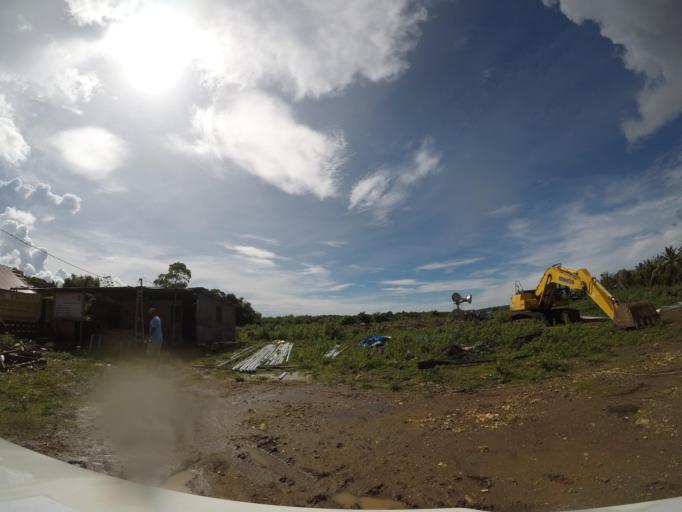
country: TL
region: Lautem
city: Lospalos
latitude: -8.5041
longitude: 127.0068
